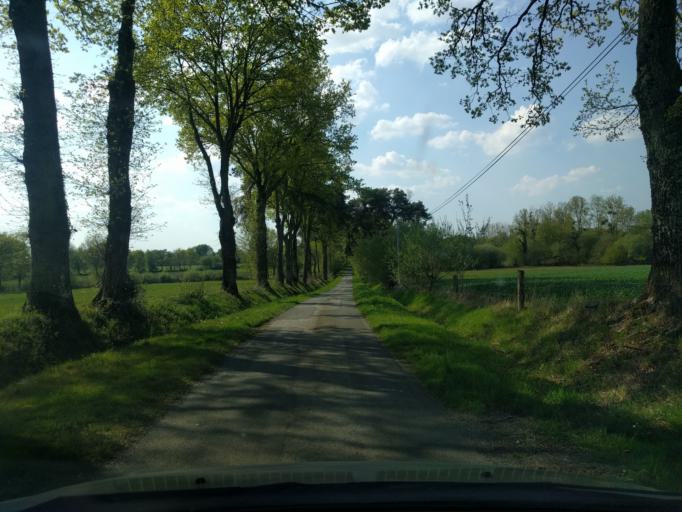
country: FR
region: Brittany
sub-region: Departement d'Ille-et-Vilaine
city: Gosne
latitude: 48.2857
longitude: -1.4457
